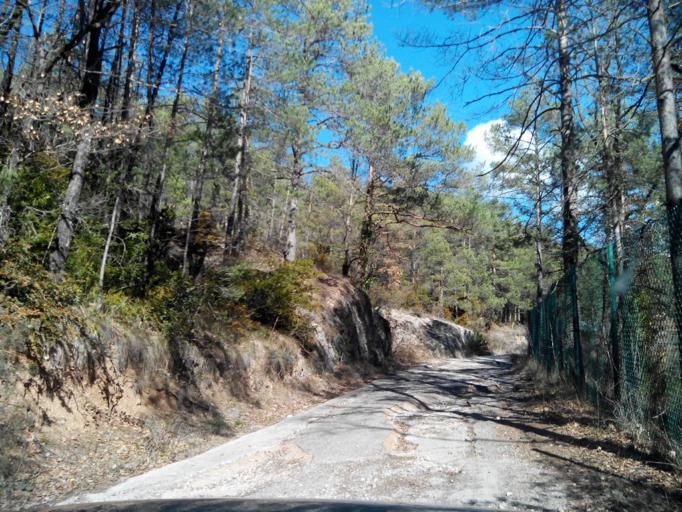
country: ES
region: Catalonia
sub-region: Provincia de Barcelona
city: Vilada
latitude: 42.1289
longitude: 1.9278
